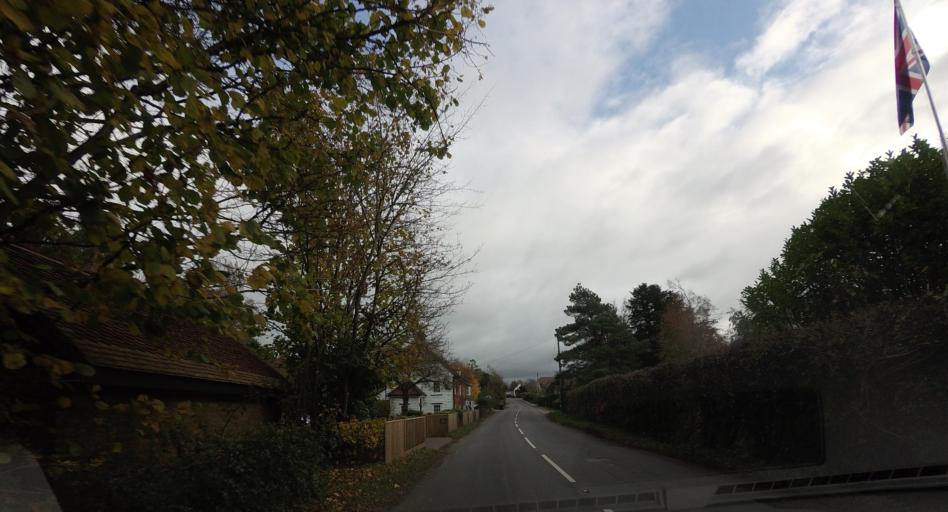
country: GB
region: England
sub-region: Kent
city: Paddock Wood
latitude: 51.1507
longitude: 0.3871
